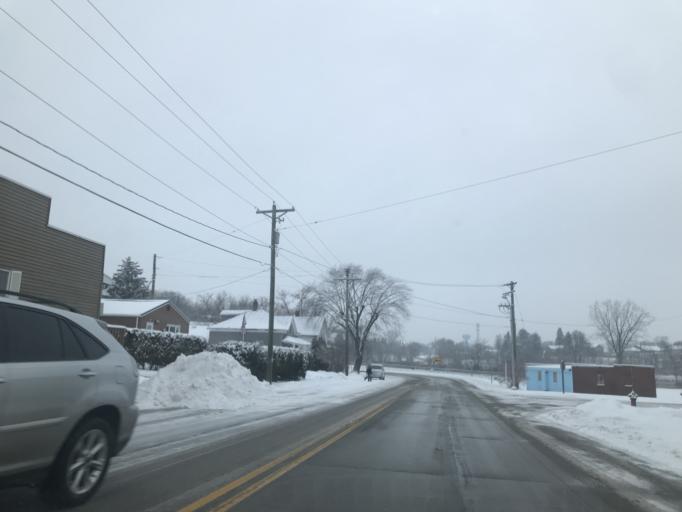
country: US
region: Wisconsin
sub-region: Oconto County
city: Oconto Falls
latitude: 44.8722
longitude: -88.1465
